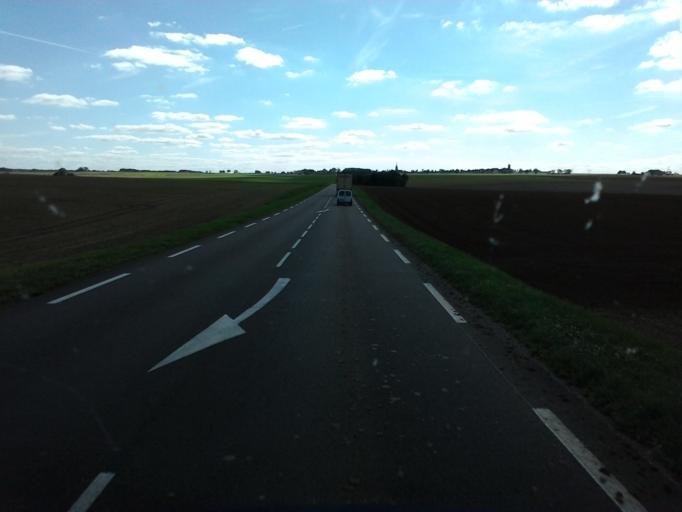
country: FR
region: Bourgogne
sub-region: Departement de la Cote-d'Or
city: Chatillon-sur-Seine
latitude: 47.7687
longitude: 4.5038
